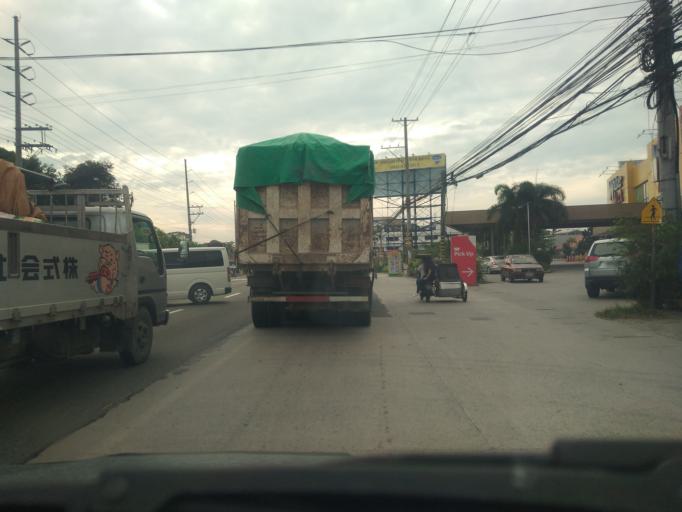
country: PH
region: Central Luzon
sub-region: Province of Pampanga
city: Magliman
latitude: 15.0491
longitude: 120.6663
